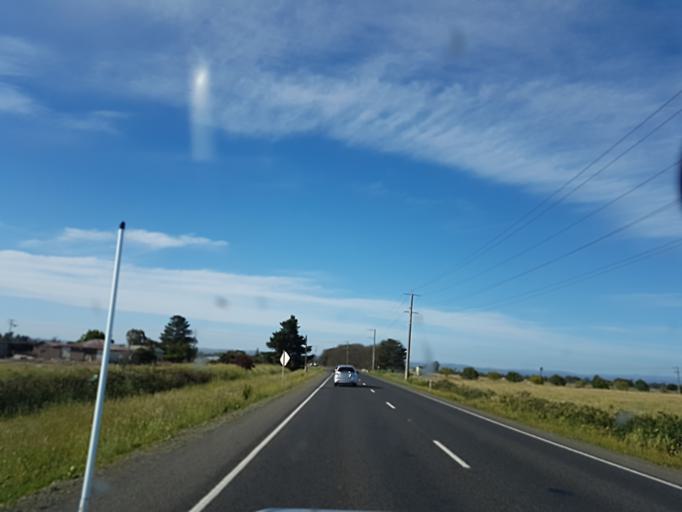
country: AU
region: Victoria
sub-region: Cardinia
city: Pakenham South
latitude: -38.1414
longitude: 145.4883
